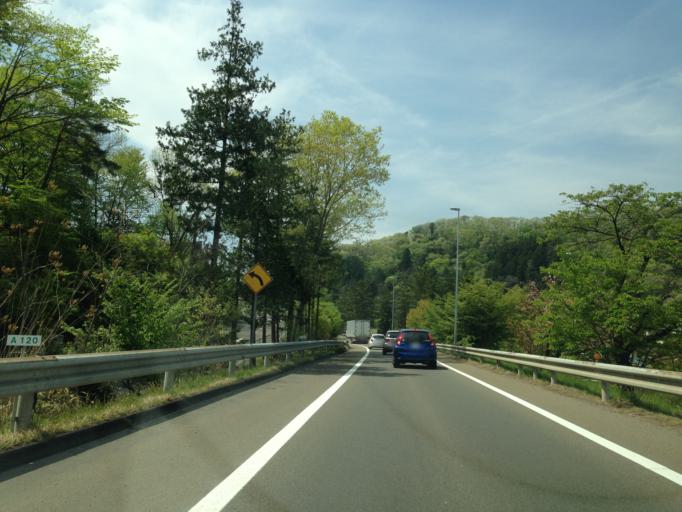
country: JP
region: Miyagi
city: Sendai
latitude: 38.2583
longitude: 140.8127
